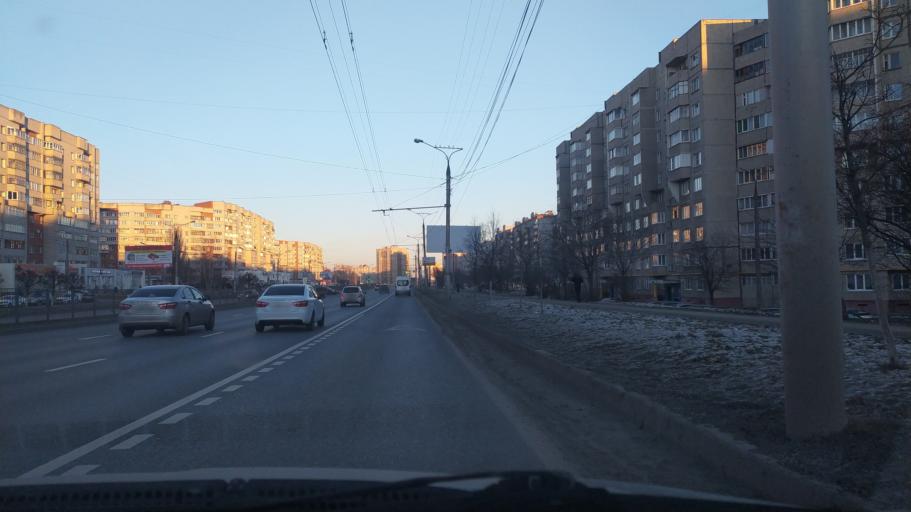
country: RU
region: Chuvashia
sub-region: Cheboksarskiy Rayon
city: Cheboksary
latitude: 56.1041
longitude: 47.3150
